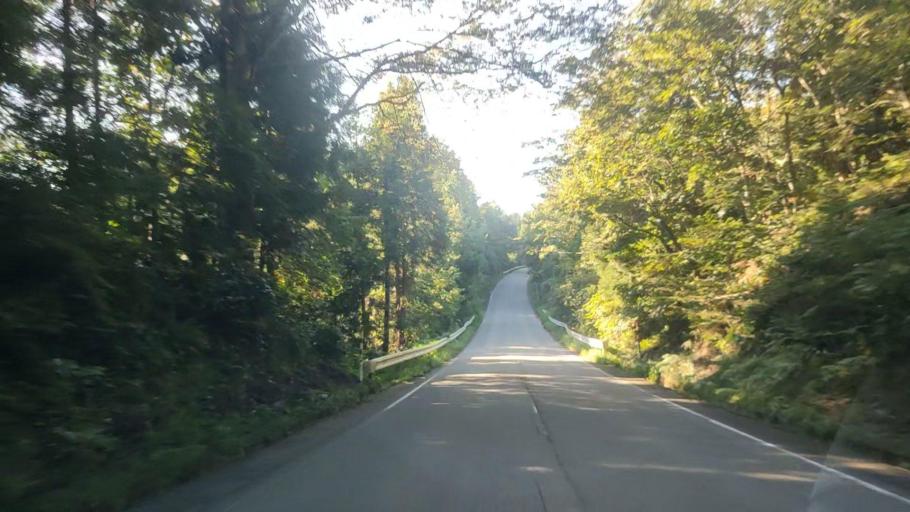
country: JP
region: Ishikawa
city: Nanao
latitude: 37.1197
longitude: 136.9379
